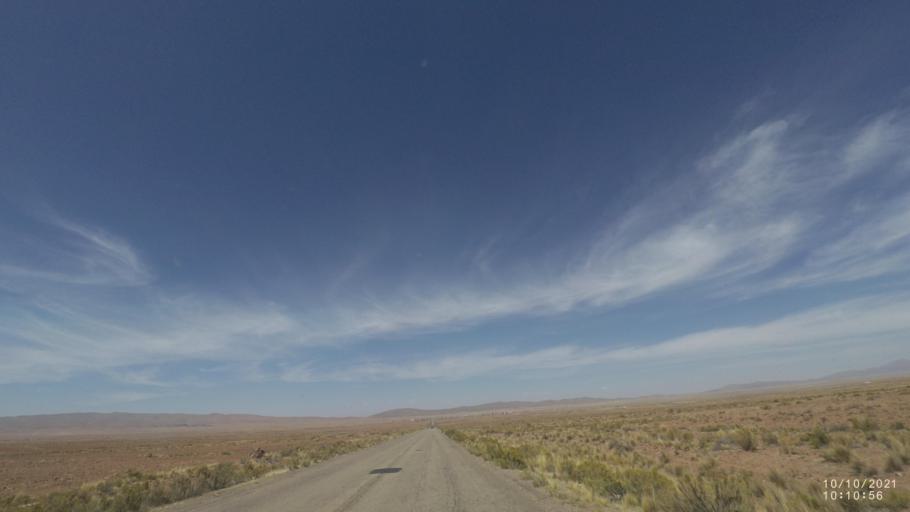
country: BO
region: La Paz
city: Eucaliptus
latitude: -17.4163
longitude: -67.4976
